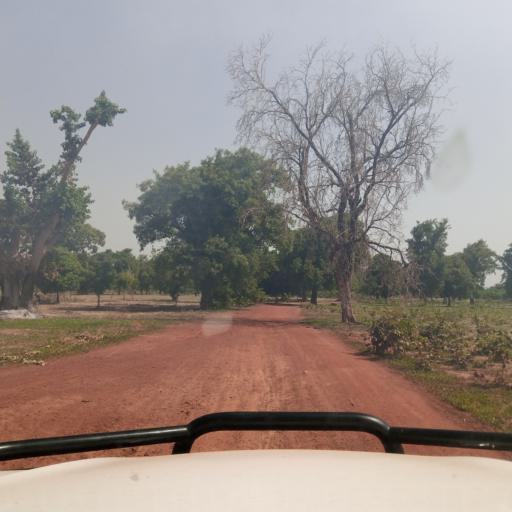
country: ML
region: Koulikoro
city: Kangaba
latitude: 12.2534
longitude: -8.6341
